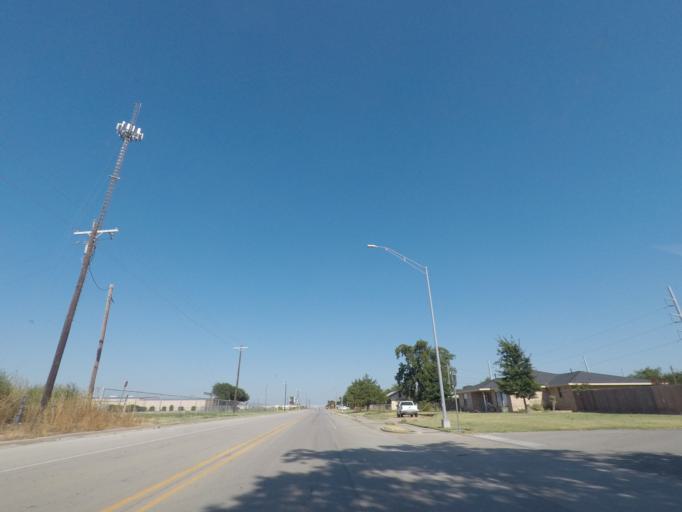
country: US
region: Texas
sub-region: Baylor County
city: Seymour
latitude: 33.5960
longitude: -99.2497
